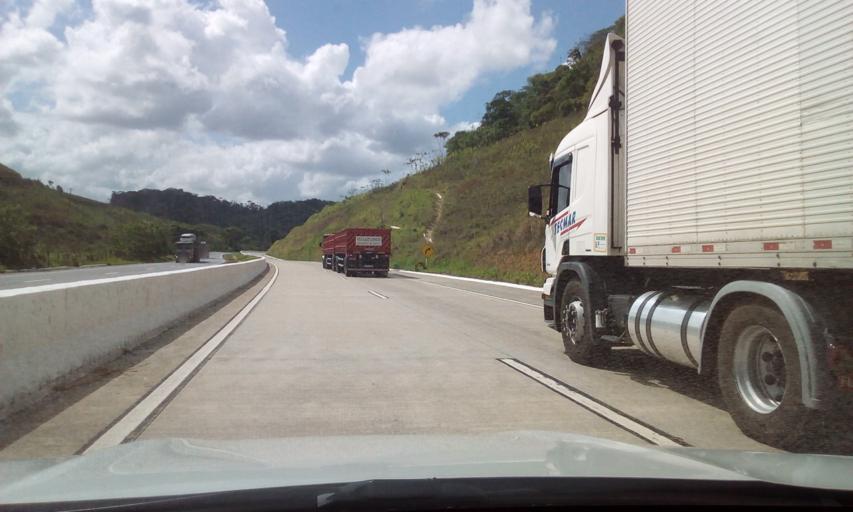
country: BR
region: Pernambuco
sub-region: Palmares
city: Palmares
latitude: -8.7513
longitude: -35.6029
